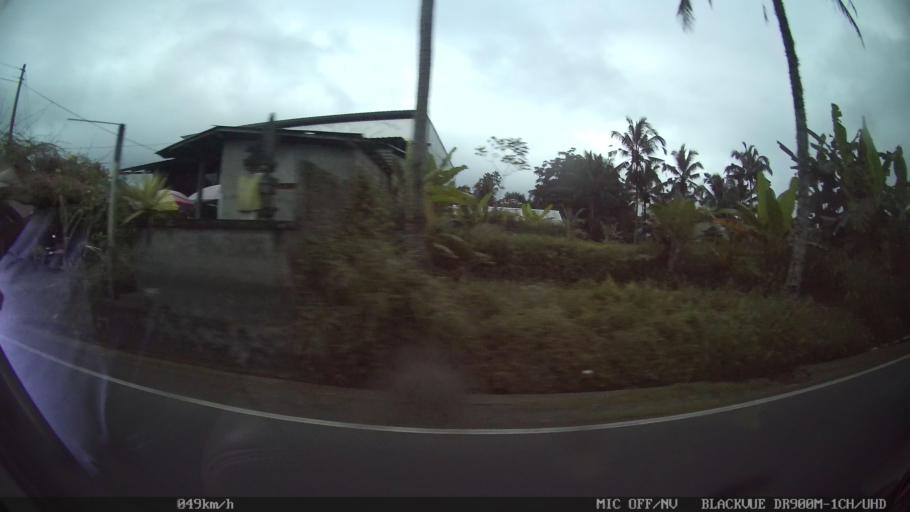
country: ID
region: Bali
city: Badung
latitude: -8.4236
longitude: 115.2449
